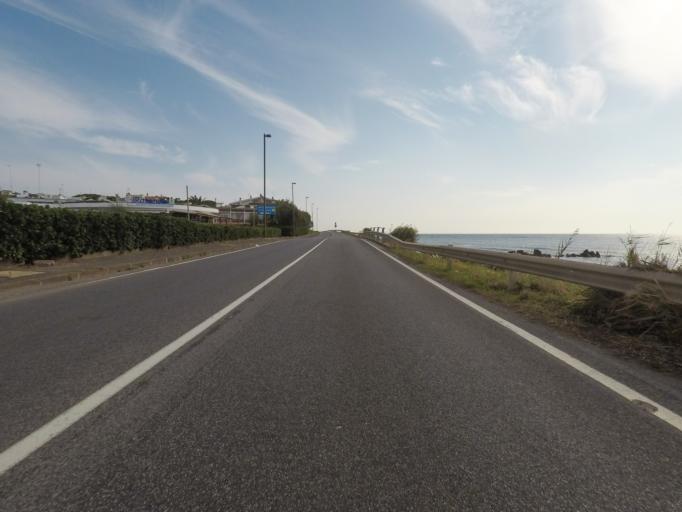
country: IT
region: Latium
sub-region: Citta metropolitana di Roma Capitale
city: Santa Marinella
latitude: 42.0435
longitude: 11.8273
